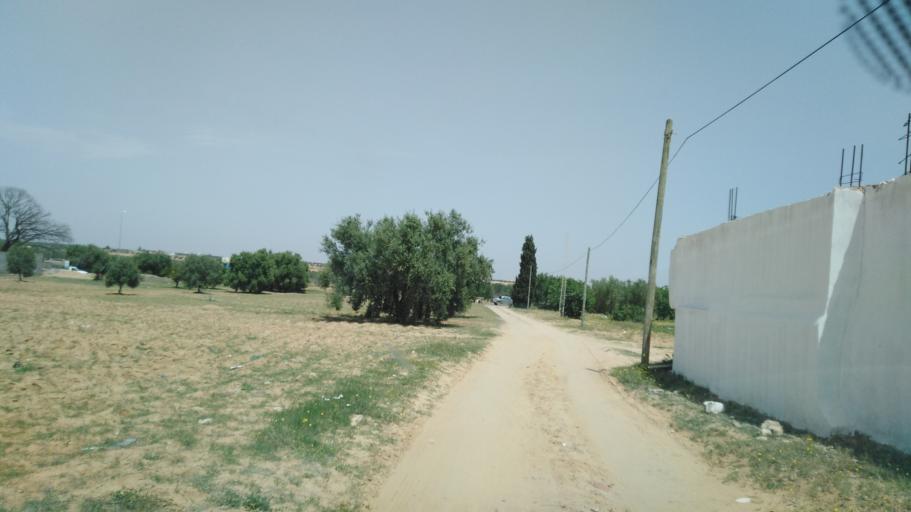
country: TN
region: Safaqis
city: Sfax
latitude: 34.7315
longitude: 10.5549
